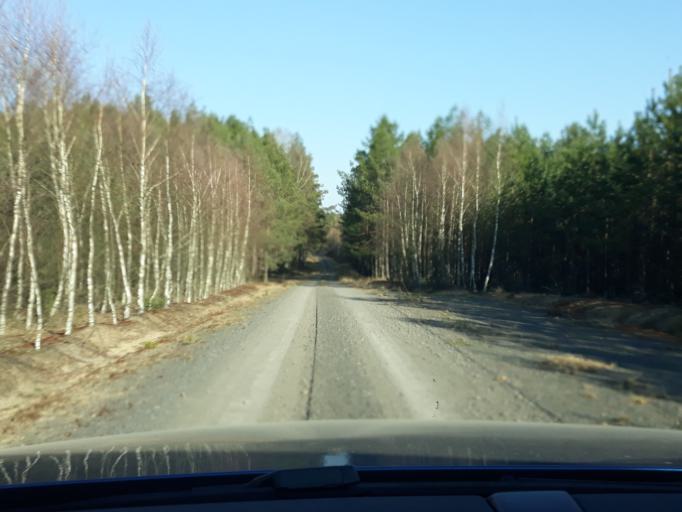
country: PL
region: Pomeranian Voivodeship
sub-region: Powiat bytowski
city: Lipnica
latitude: 53.9135
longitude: 17.4888
